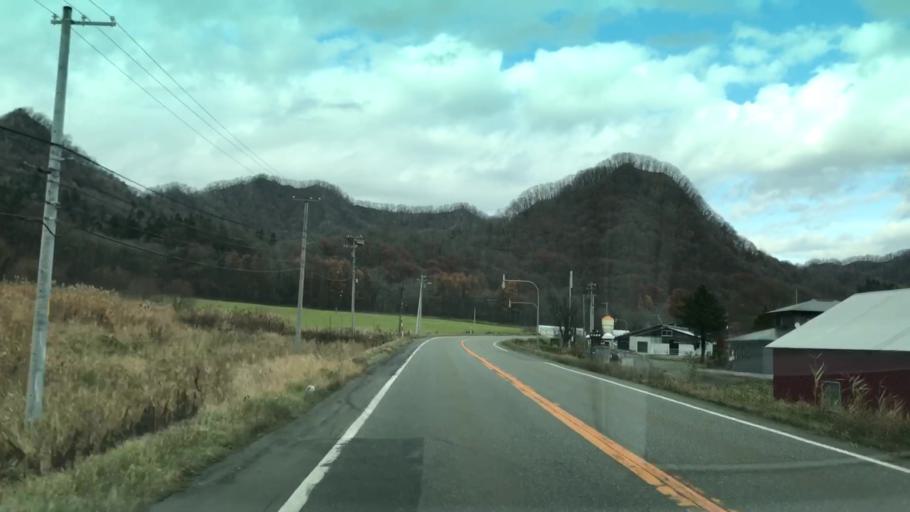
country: JP
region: Hokkaido
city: Shizunai-furukawacho
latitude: 42.8031
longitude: 142.3978
